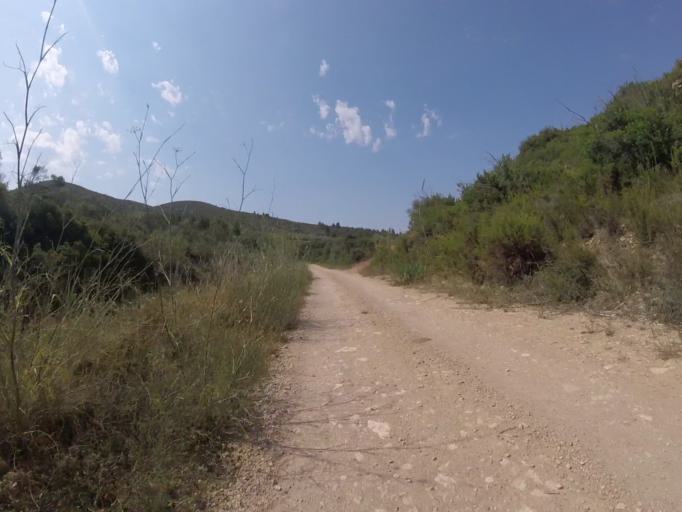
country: ES
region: Valencia
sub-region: Provincia de Castello
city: Cuevas de Vinroma
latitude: 40.3102
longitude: 0.1765
